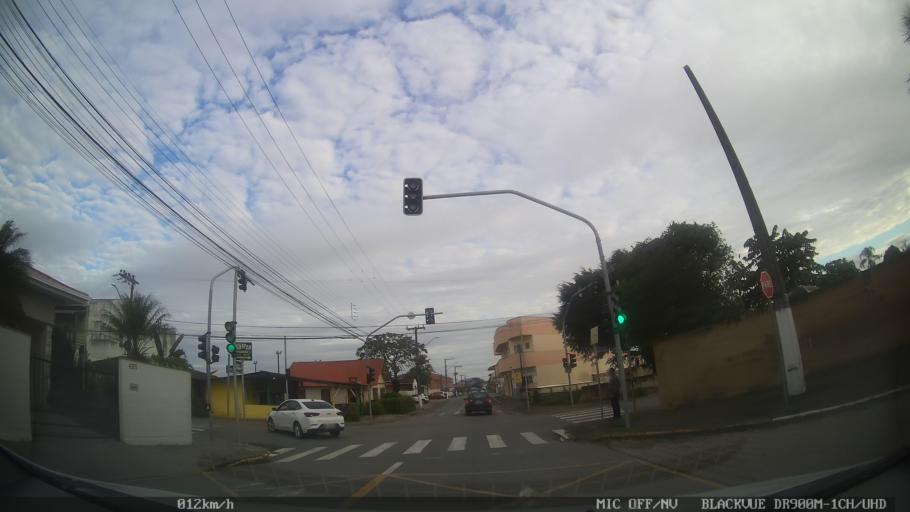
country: BR
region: Santa Catarina
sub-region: Barra Velha
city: Barra Velha
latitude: -26.6317
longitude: -48.6867
